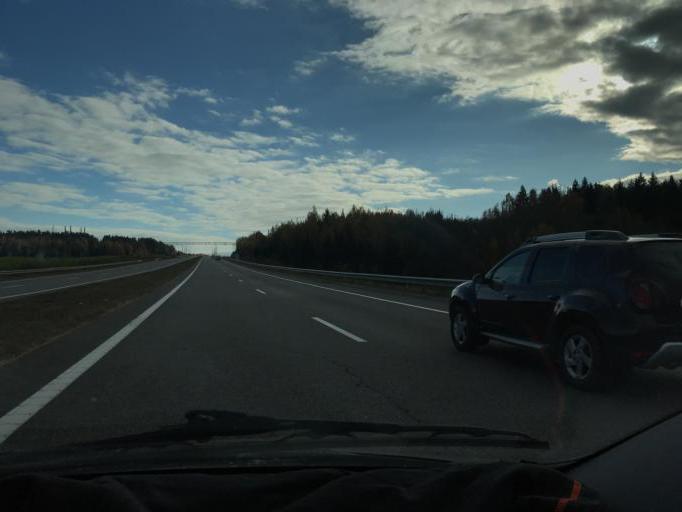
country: BY
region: Minsk
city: Lahoysk
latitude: 54.1862
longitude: 27.8170
